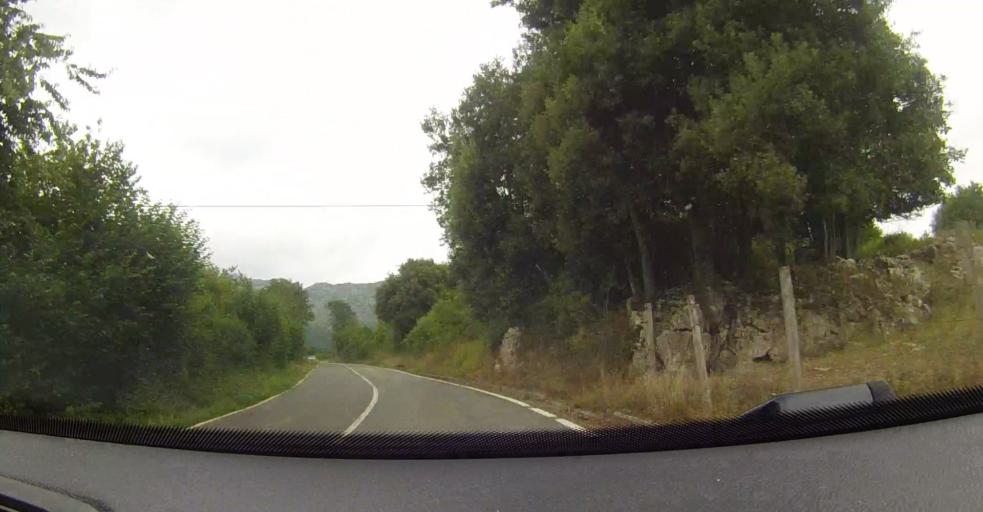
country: ES
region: Cantabria
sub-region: Provincia de Cantabria
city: Rasines
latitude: 43.2591
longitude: -3.3701
